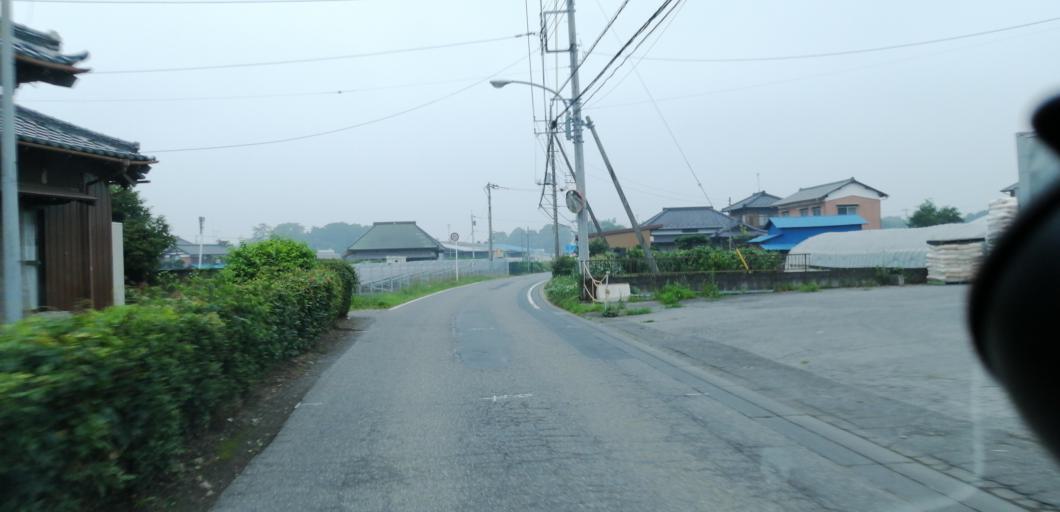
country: JP
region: Ibaraki
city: Iwai
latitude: 36.0298
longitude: 139.8393
